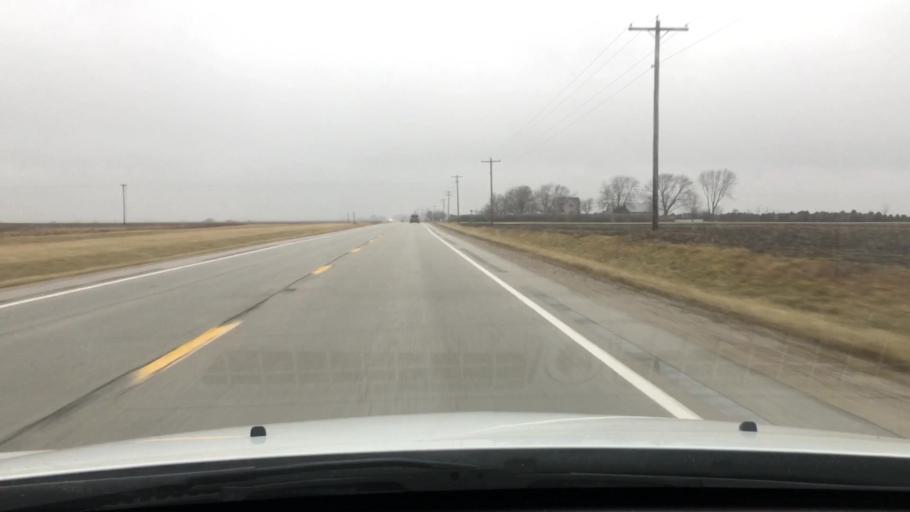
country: US
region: Illinois
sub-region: Livingston County
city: Flanagan
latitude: 40.8718
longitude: -88.8130
